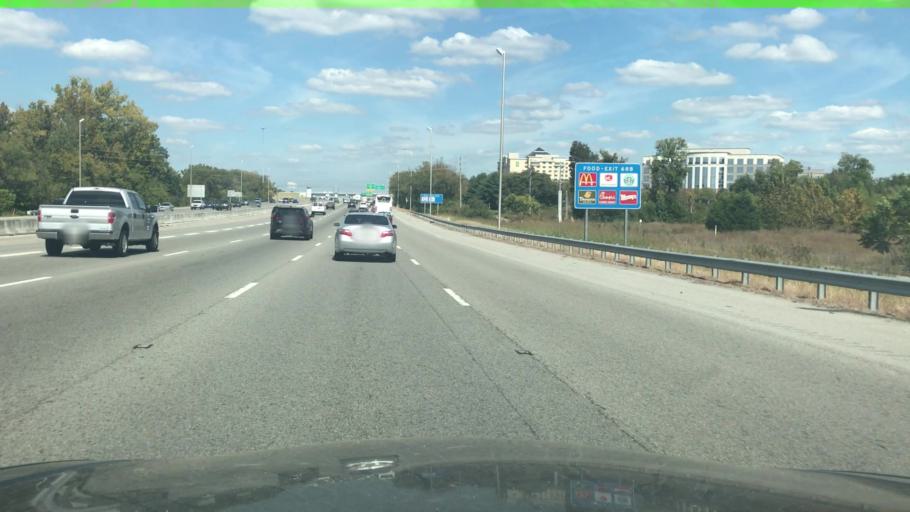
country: US
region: Tennessee
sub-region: Williamson County
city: Franklin
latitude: 35.9397
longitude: -86.8167
